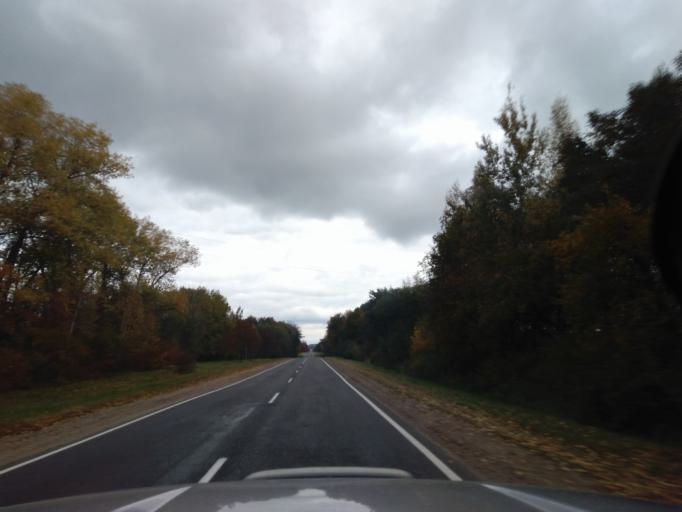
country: BY
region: Minsk
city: Slutsk
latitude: 53.2226
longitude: 27.3682
